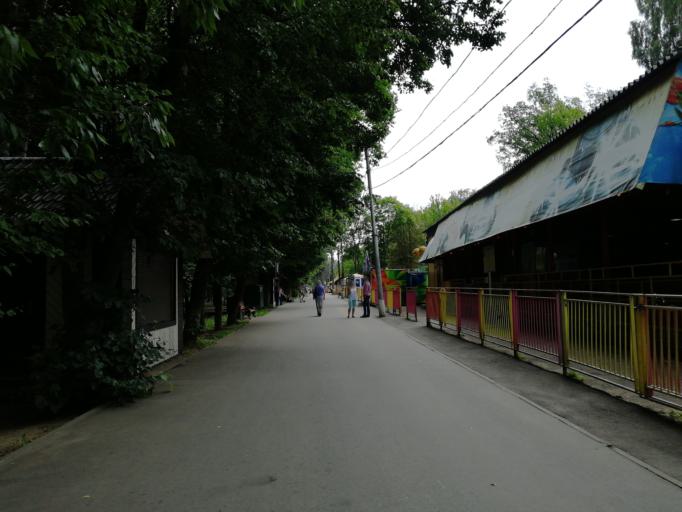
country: RU
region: Tula
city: Tula
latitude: 54.1826
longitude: 37.5894
